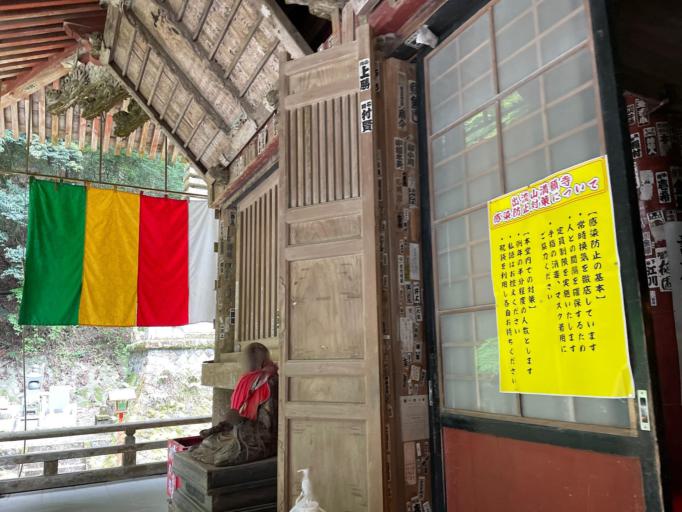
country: JP
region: Tochigi
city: Tanuma
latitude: 36.4754
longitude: 139.5896
